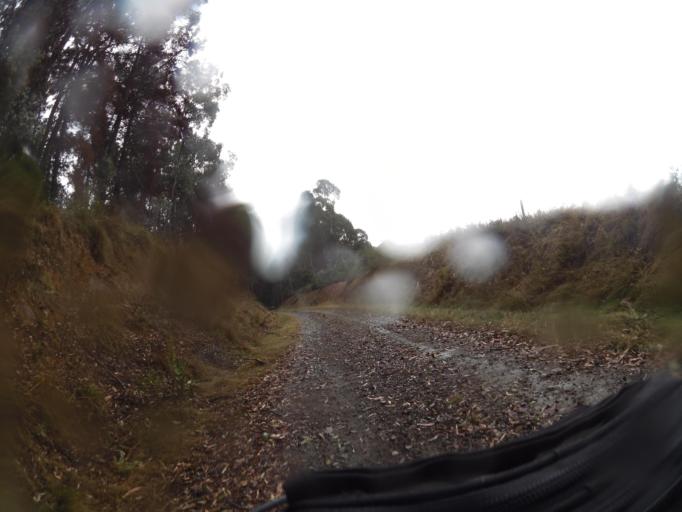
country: AU
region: New South Wales
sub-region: Greater Hume Shire
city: Holbrook
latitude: -36.2169
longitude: 147.5663
